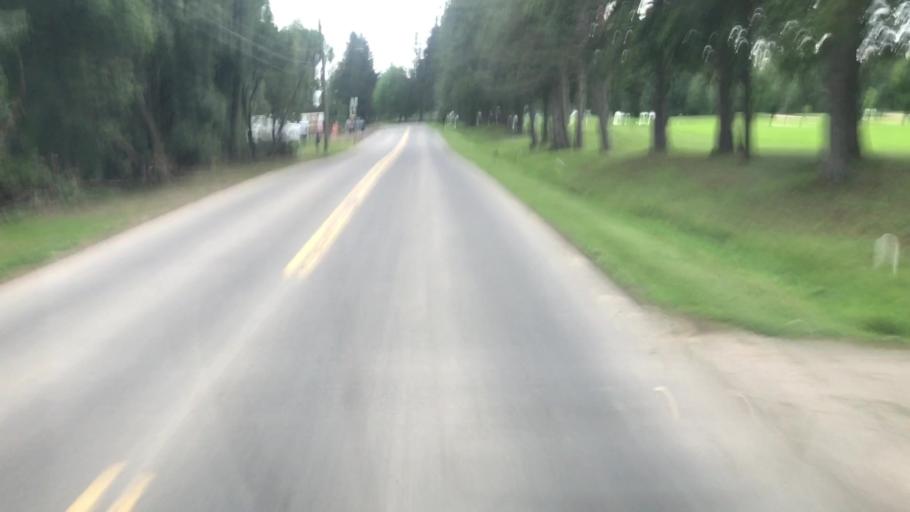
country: US
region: New York
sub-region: Cayuga County
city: Melrose Park
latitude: 42.9065
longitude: -76.5292
